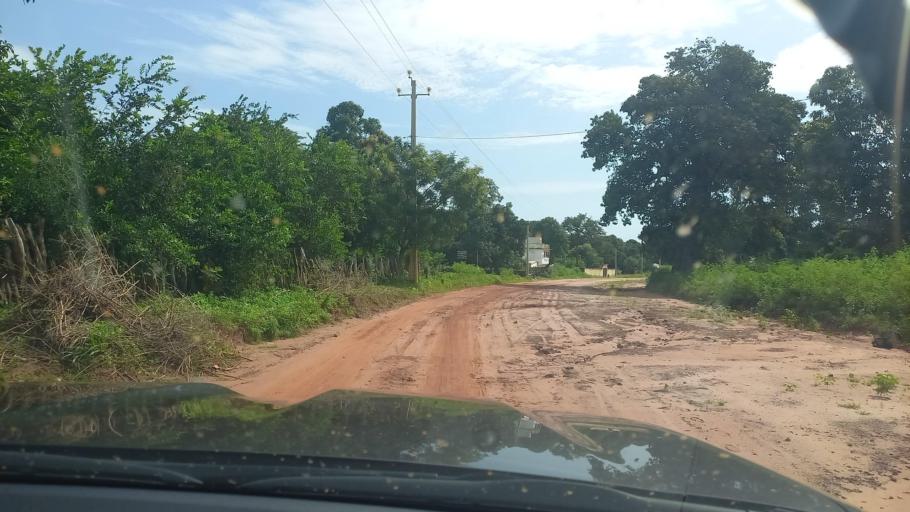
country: SN
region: Ziguinchor
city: Ziguinchor
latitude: 12.6730
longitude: -16.2107
